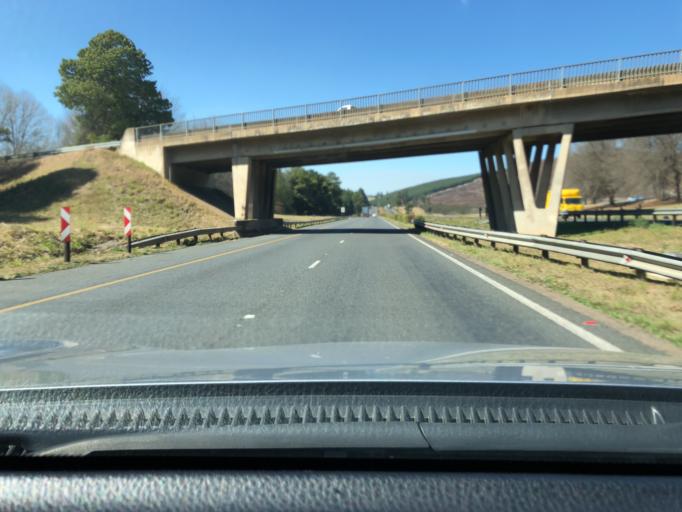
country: ZA
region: KwaZulu-Natal
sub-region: uMgungundlovu District Municipality
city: Howick
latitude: -29.3590
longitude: 30.0961
